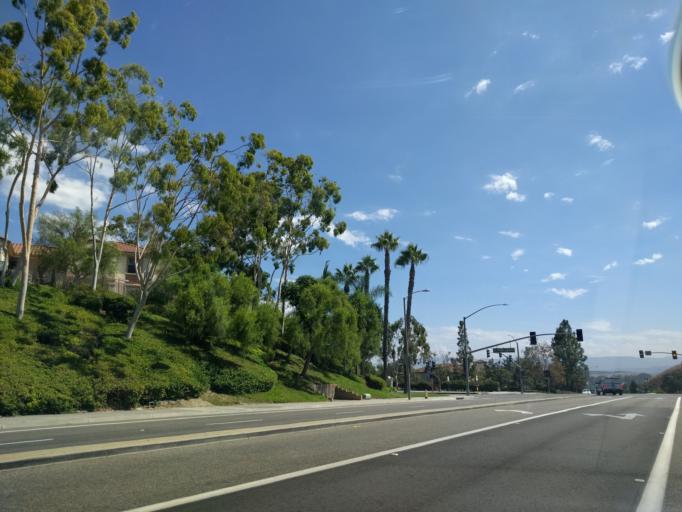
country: US
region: California
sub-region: Orange County
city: Laguna Niguel
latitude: 33.5248
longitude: -117.6864
